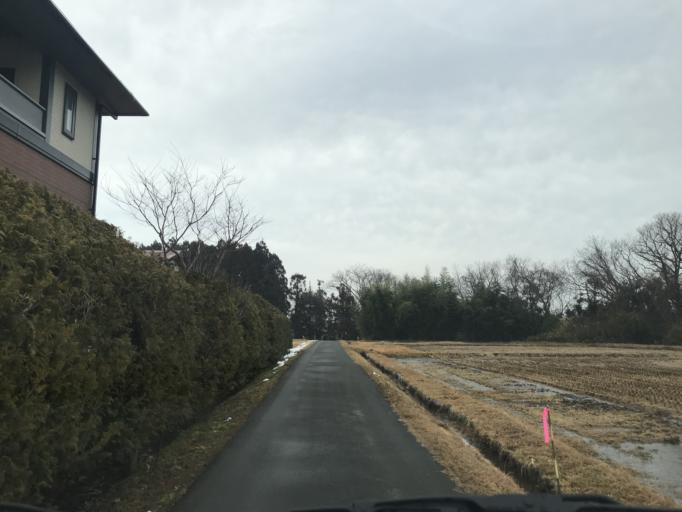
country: JP
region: Iwate
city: Mizusawa
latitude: 39.1826
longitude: 141.1395
